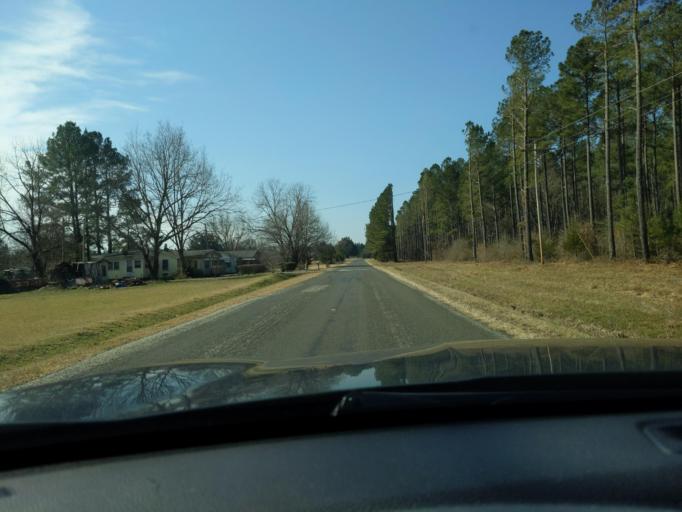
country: US
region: South Carolina
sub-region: Abbeville County
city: Calhoun Falls
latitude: 34.0826
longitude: -82.5655
